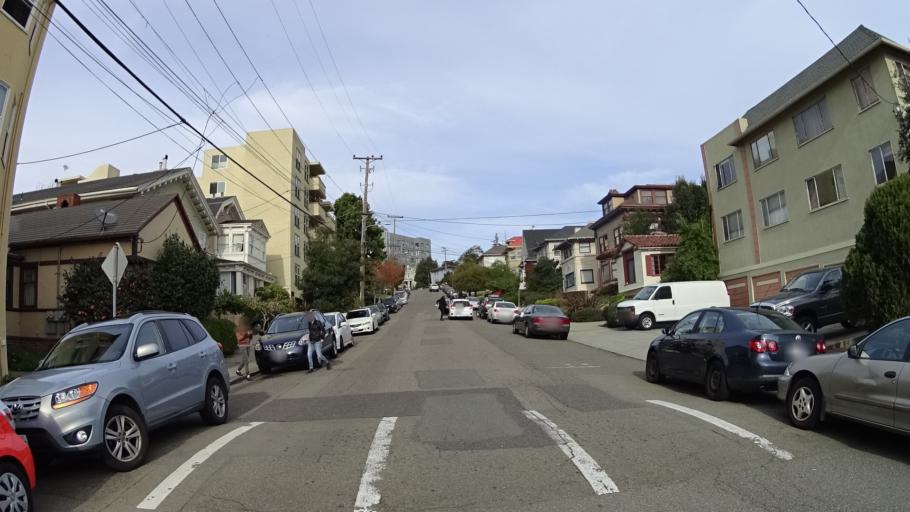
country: US
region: California
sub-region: Alameda County
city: Oakland
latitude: 37.8100
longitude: -122.2582
